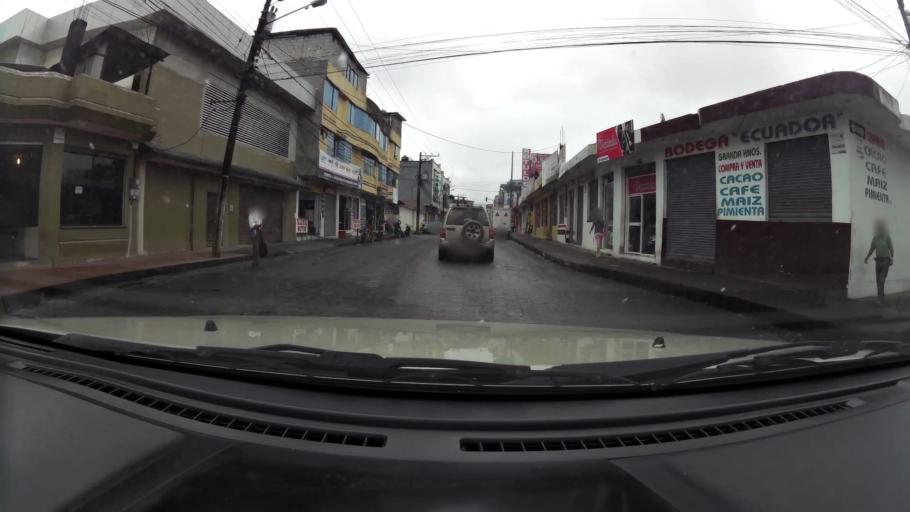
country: EC
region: Santo Domingo de los Tsachilas
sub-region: Canton Santo Domingo de los Colorados
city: Santo Domingo de los Colorados
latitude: -0.2555
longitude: -79.1755
